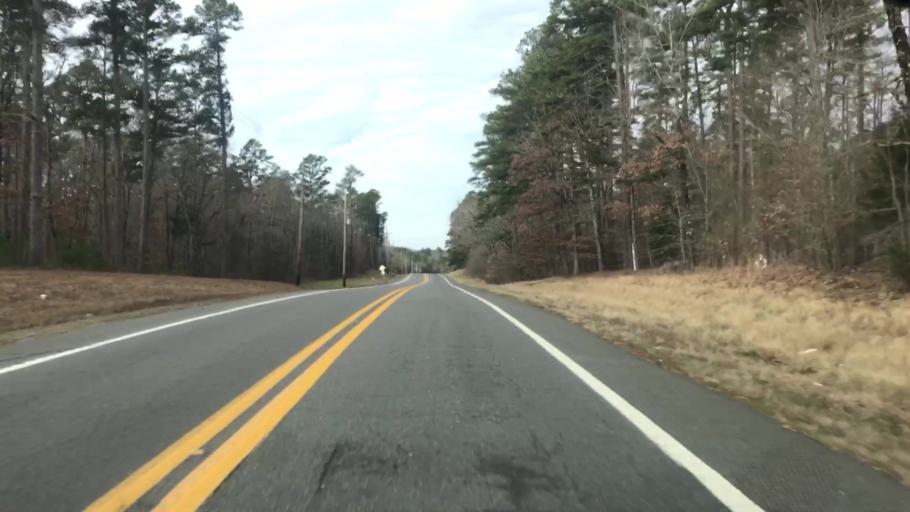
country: US
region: Arkansas
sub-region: Montgomery County
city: Mount Ida
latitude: 34.6087
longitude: -93.6765
